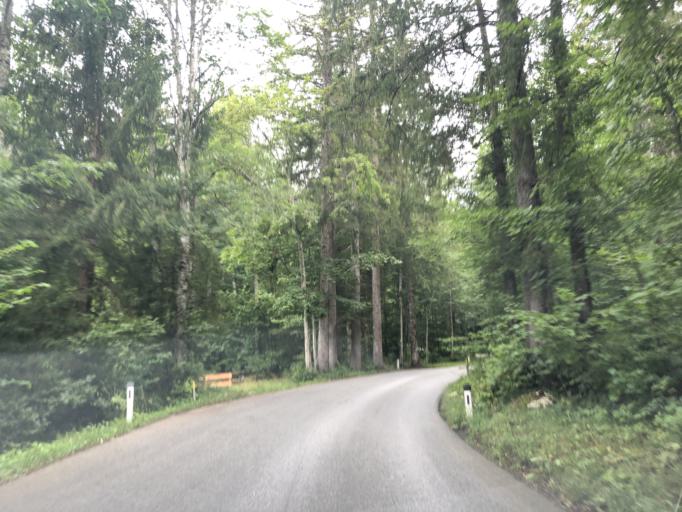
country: AT
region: Tyrol
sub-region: Politischer Bezirk Kufstein
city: Scheffau am Wilden Kaiser
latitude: 47.5342
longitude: 12.2463
